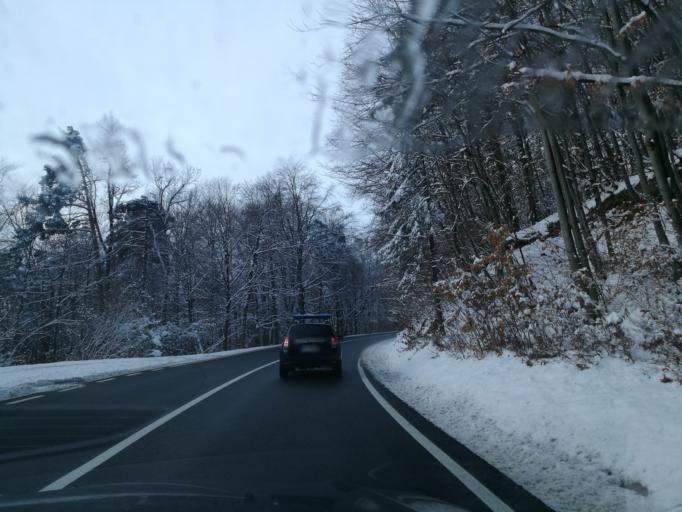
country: RO
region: Brasov
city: Brasov
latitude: 45.6226
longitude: 25.5476
